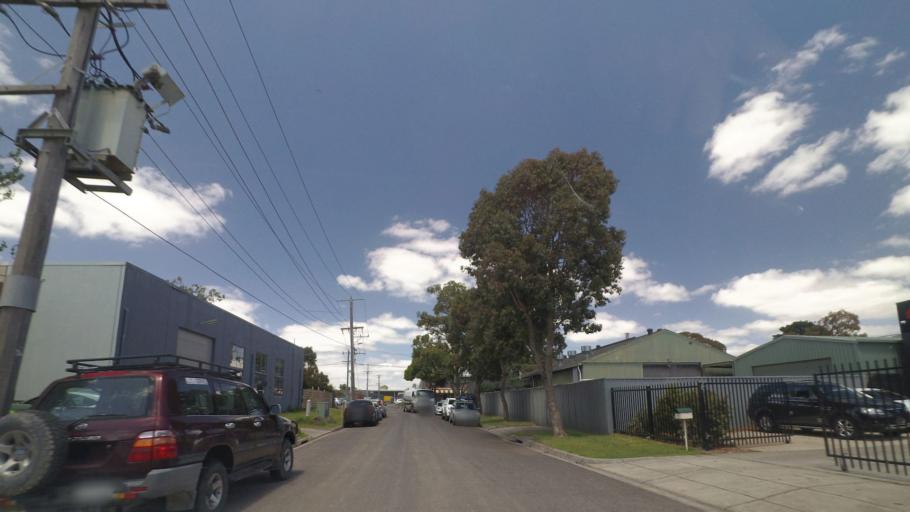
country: AU
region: Victoria
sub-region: Maroondah
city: Bayswater North
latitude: -37.8206
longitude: 145.2918
